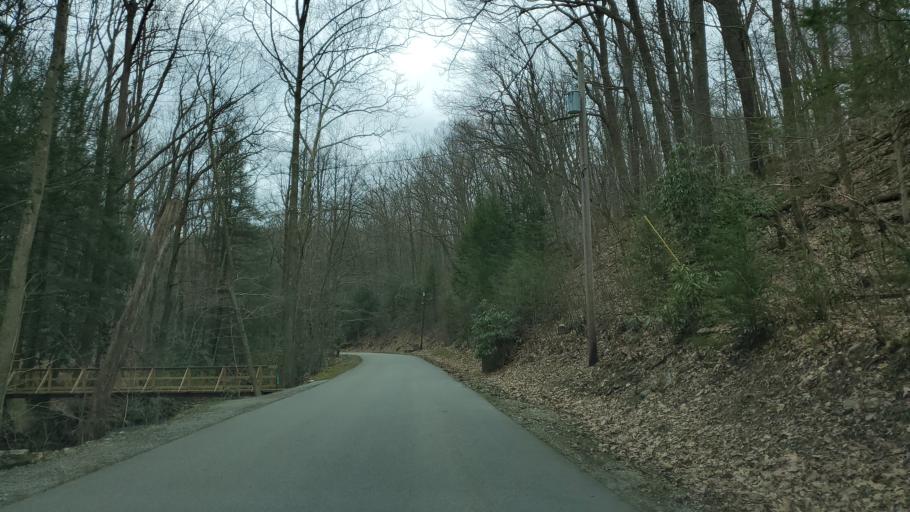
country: US
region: Pennsylvania
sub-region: Westmoreland County
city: Ligonier
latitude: 40.1611
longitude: -79.2322
